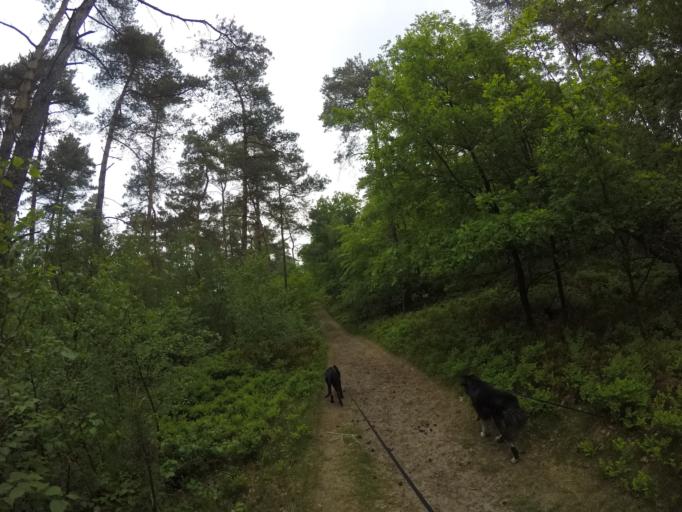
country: NL
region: Gelderland
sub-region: Gemeente Rheden
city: Velp
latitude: 52.0250
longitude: 5.9945
